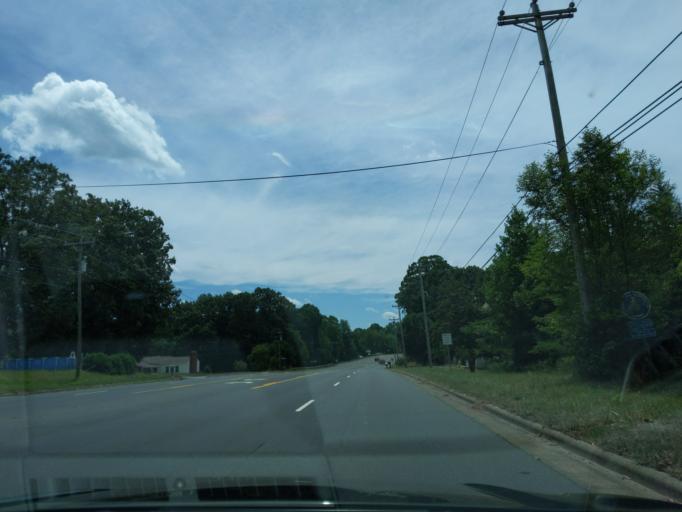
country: US
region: North Carolina
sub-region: Stanly County
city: Albemarle
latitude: 35.4102
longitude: -80.2034
